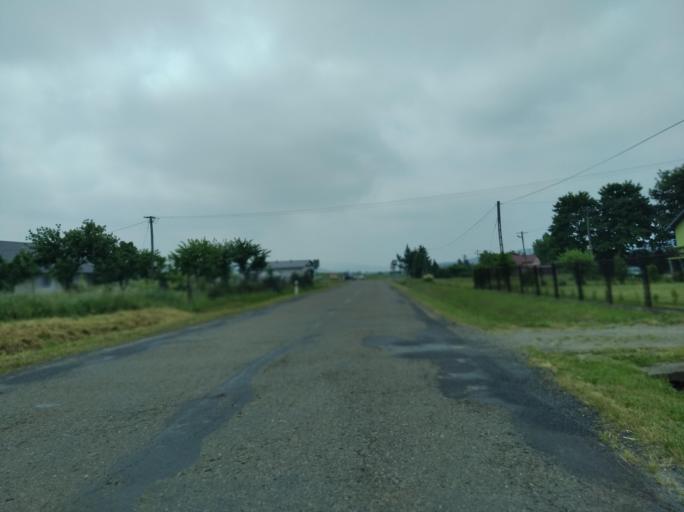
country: PL
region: Subcarpathian Voivodeship
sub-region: Powiat krosnienski
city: Sieniawa
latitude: 49.5665
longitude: 21.9233
